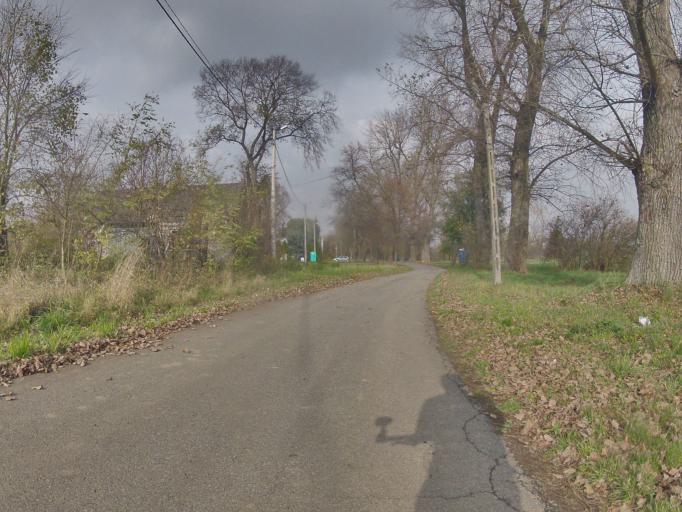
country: PL
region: Lesser Poland Voivodeship
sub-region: Powiat wielicki
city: Wegrzce Wielkie
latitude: 50.0558
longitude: 20.1122
